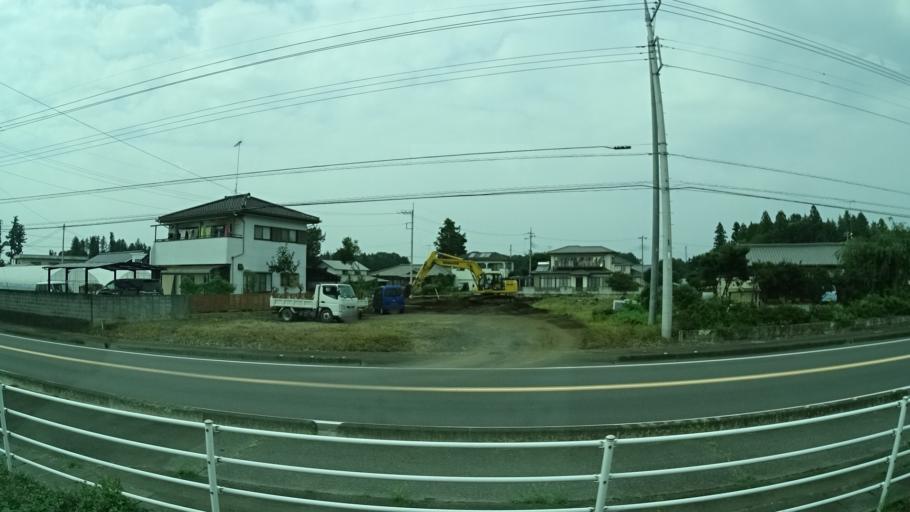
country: JP
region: Tochigi
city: Mashiko
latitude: 36.4553
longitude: 140.0648
